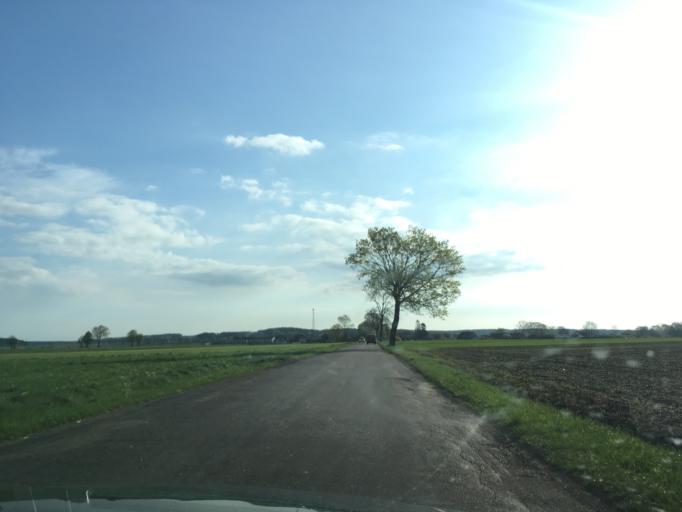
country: PL
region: Warmian-Masurian Voivodeship
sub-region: Powiat nidzicki
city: Kozlowo
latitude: 53.4066
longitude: 20.3219
